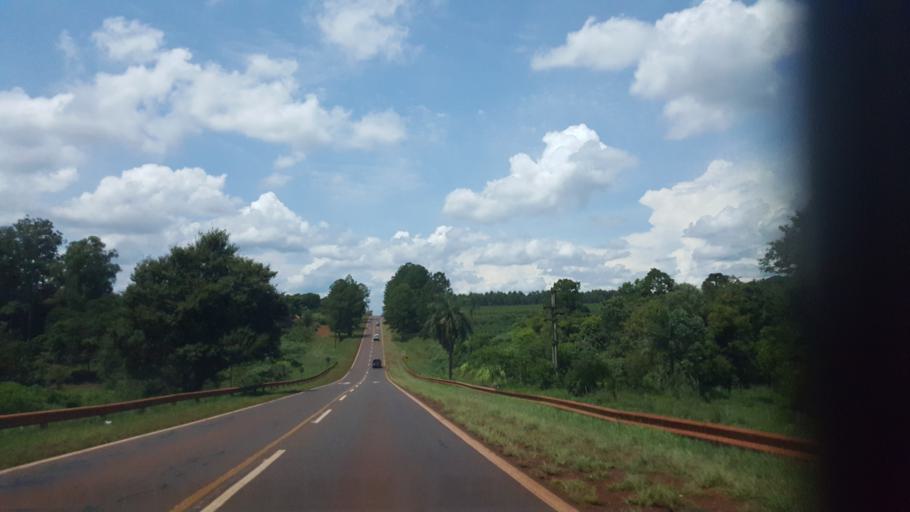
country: AR
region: Misiones
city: Puerto Rico
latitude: -26.8206
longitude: -54.9966
